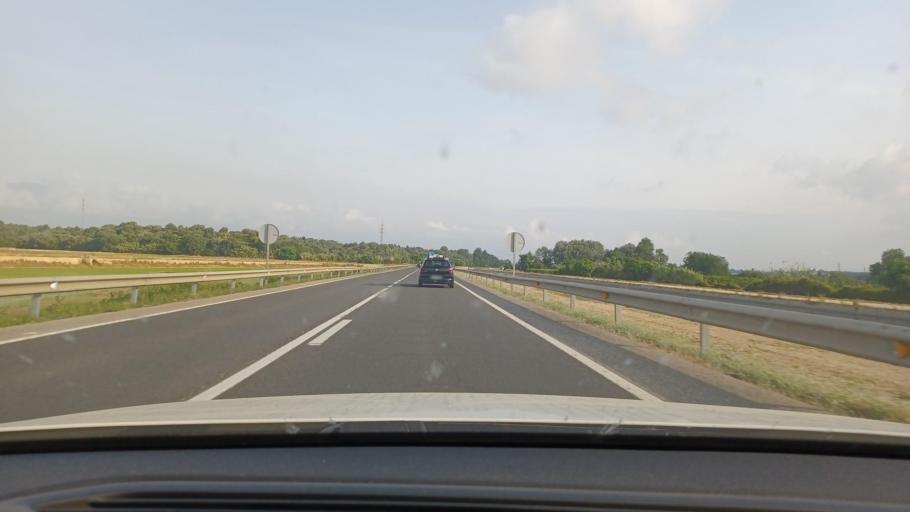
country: ES
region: Catalonia
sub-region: Provincia de Tarragona
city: Masdenverge
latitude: 40.7571
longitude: 0.5378
